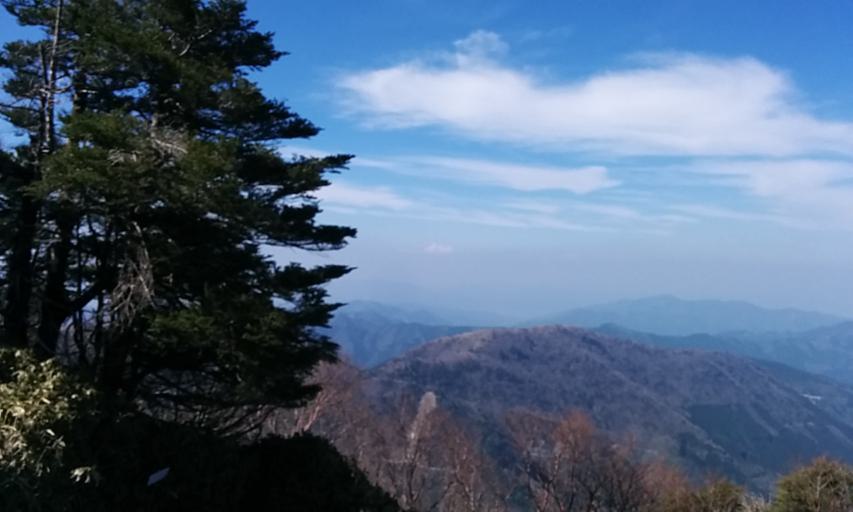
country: JP
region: Tokushima
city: Wakimachi
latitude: 33.8560
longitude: 134.0958
